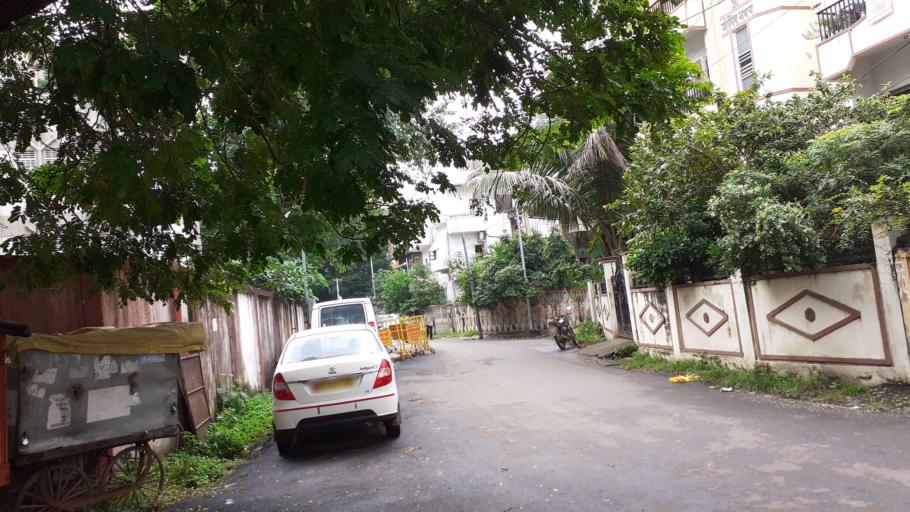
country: IN
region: Maharashtra
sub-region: Nagpur Division
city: Nagpur
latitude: 21.1300
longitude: 79.1137
